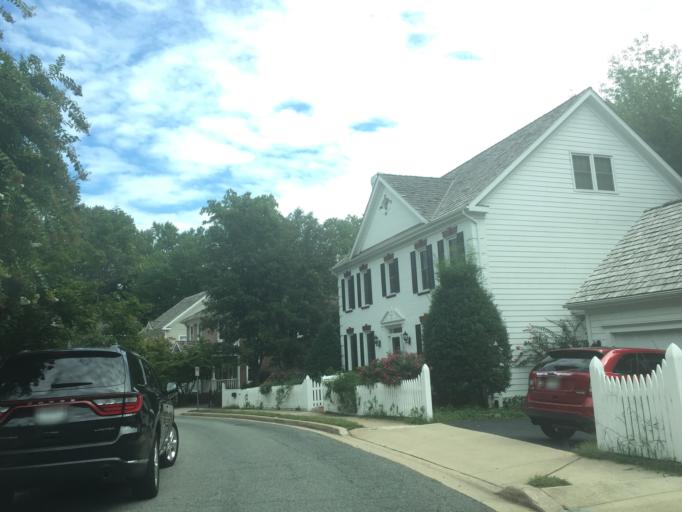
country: US
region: Maryland
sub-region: Montgomery County
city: North Potomac
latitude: 39.1204
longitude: -77.2426
